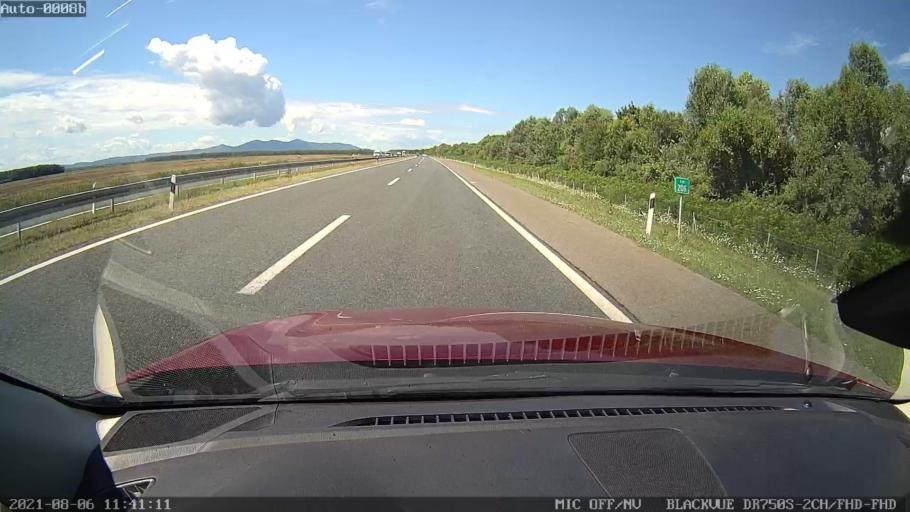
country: HR
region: Brodsko-Posavska
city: Sibinj
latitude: 45.1679
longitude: 17.8761
